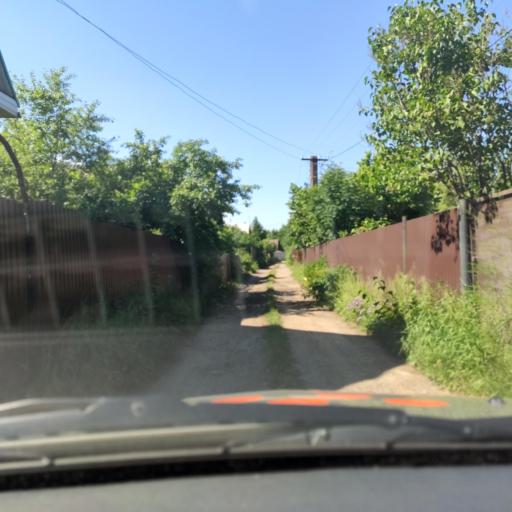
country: RU
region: Bashkortostan
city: Iglino
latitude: 54.7866
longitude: 56.1931
